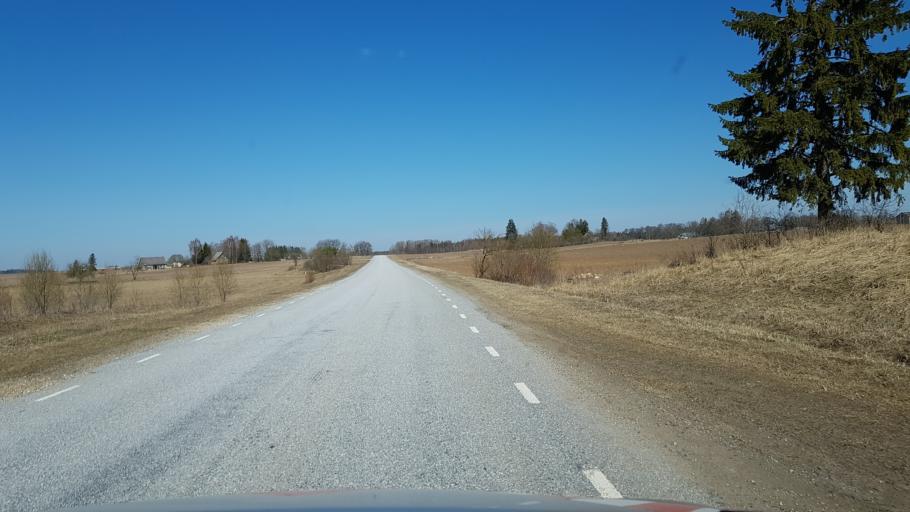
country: EE
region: Jaervamaa
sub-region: Koeru vald
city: Koeru
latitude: 59.0309
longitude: 26.0907
